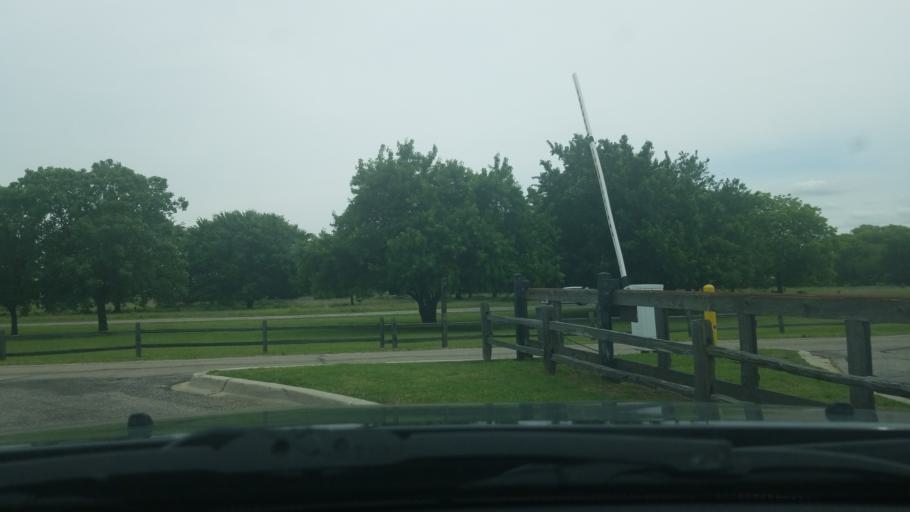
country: US
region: Texas
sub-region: Denton County
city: Lake Dallas
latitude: 33.1063
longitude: -97.0020
